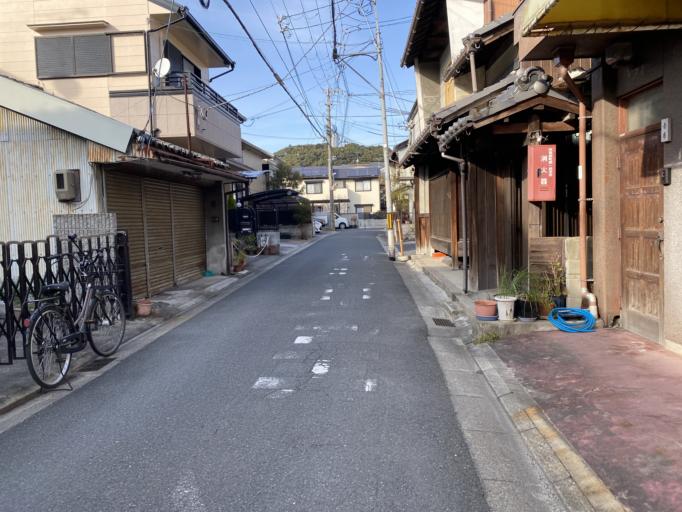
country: JP
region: Nara
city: Nara-shi
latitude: 34.6906
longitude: 135.8298
